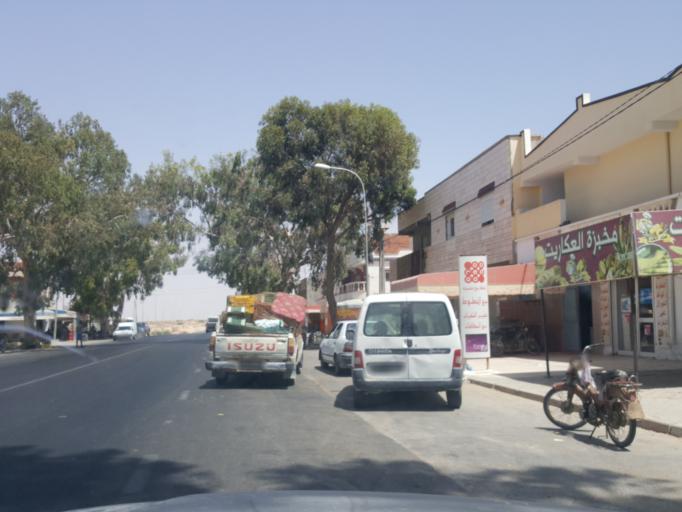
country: TN
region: Safaqis
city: Skhira
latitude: 34.1054
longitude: 9.9833
